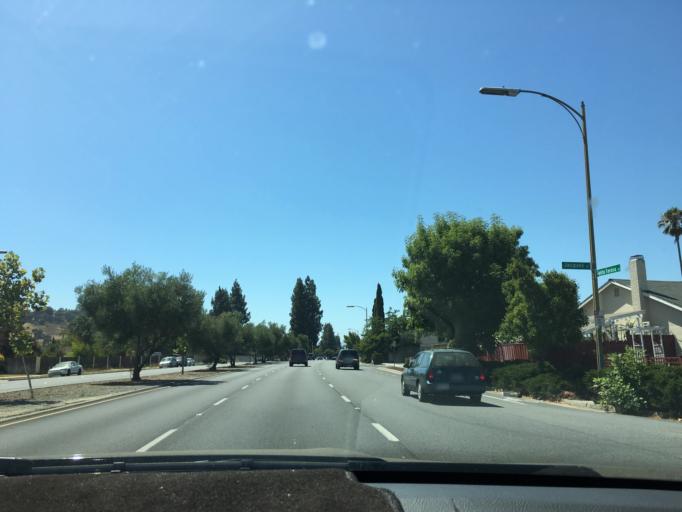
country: US
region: California
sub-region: Santa Clara County
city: Seven Trees
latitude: 37.2370
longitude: -121.8423
